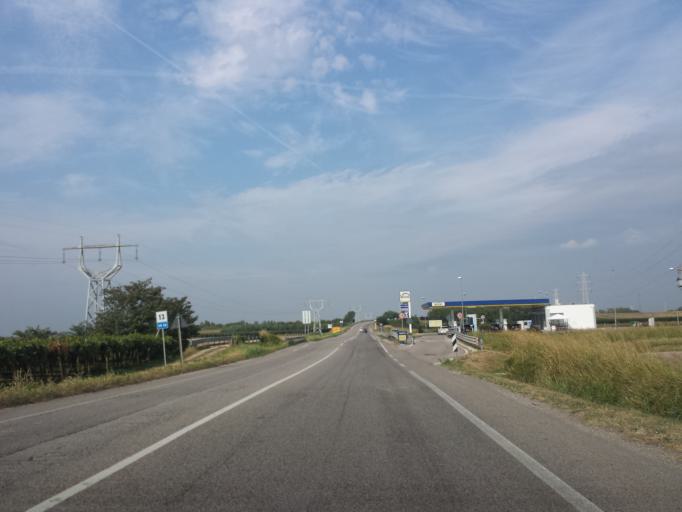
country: IT
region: Veneto
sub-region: Provincia di Verona
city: San Bonifacio
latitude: 45.3859
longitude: 11.2752
